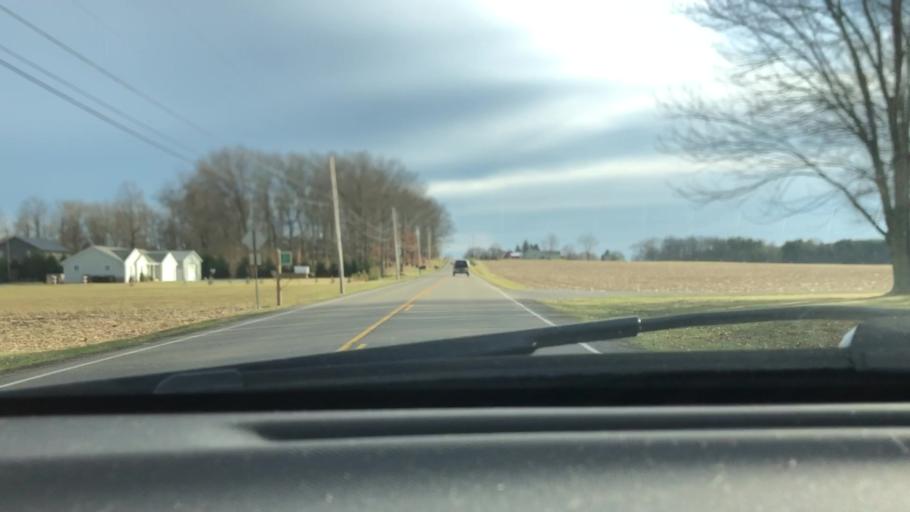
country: US
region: Ohio
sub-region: Wayne County
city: Dalton
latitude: 40.7918
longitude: -81.7454
